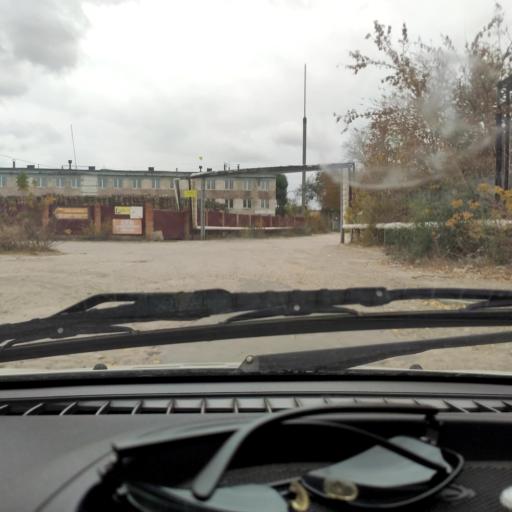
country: RU
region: Samara
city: Tol'yatti
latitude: 53.5314
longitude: 49.4518
